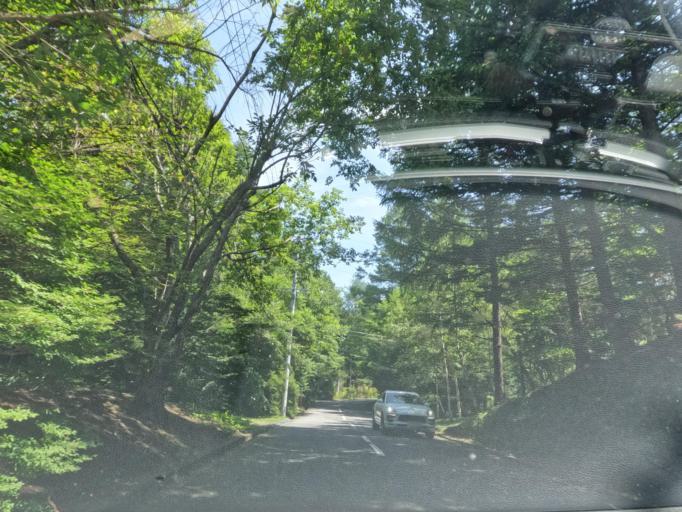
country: JP
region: Nagano
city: Komoro
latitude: 36.3570
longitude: 138.5955
